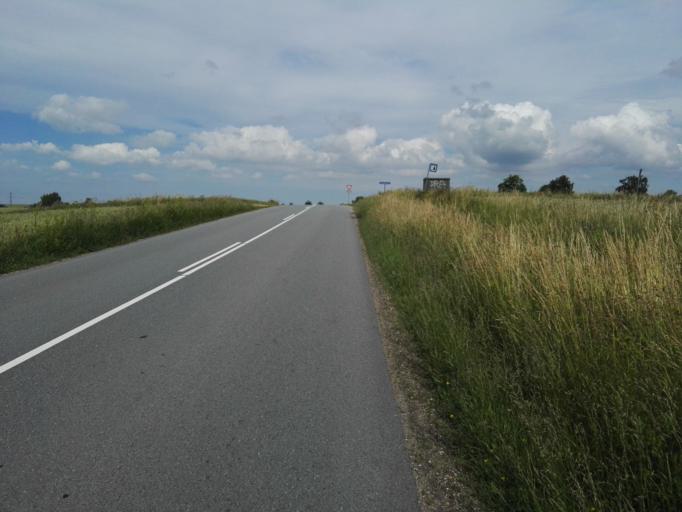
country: DK
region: Capital Region
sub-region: Frederikssund Kommune
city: Slangerup
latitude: 55.8626
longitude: 12.1787
